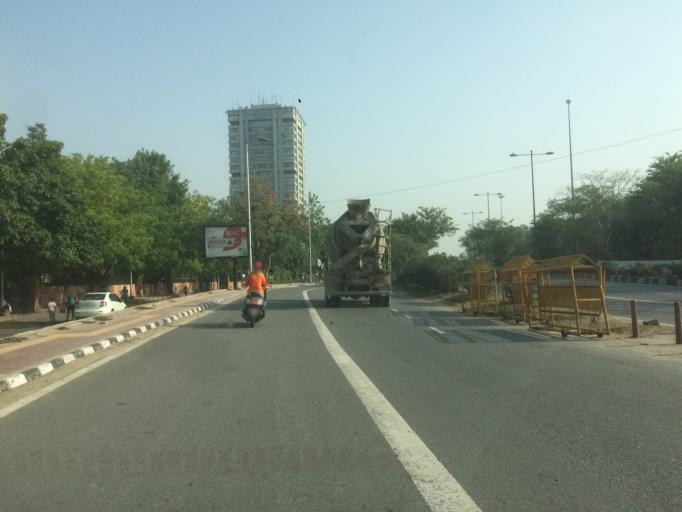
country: IN
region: NCT
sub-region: New Delhi
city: New Delhi
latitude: 28.6254
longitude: 77.2468
